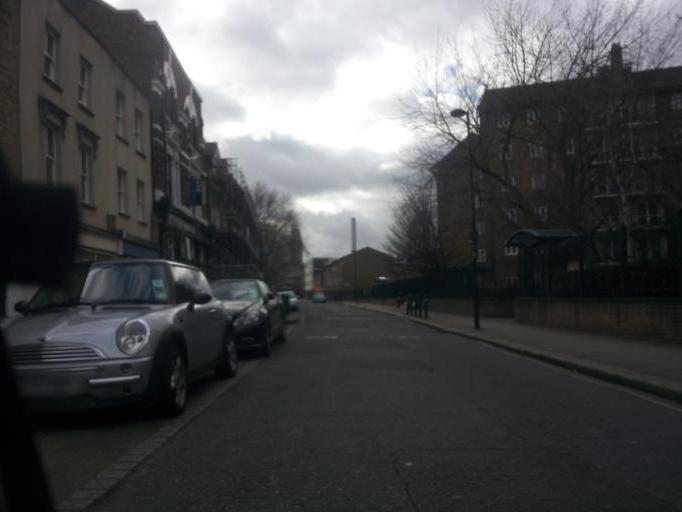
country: GB
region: England
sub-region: Greater London
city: Lambeth
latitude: 51.4946
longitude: -0.1140
